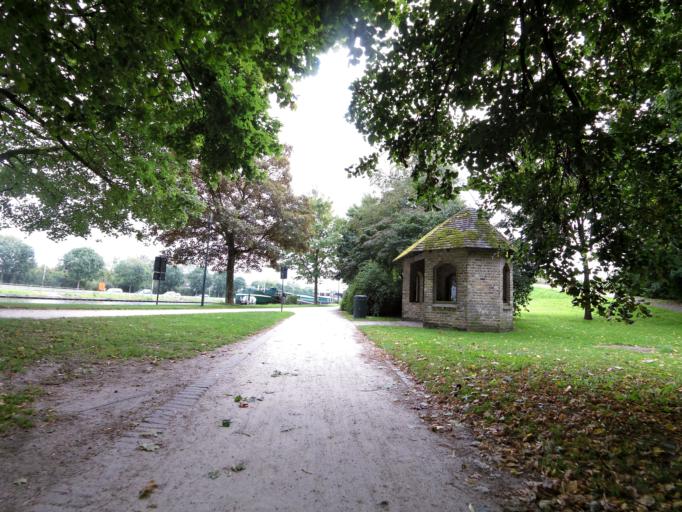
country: BE
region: Flanders
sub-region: Provincie West-Vlaanderen
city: Brugge
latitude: 51.2205
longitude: 3.2339
